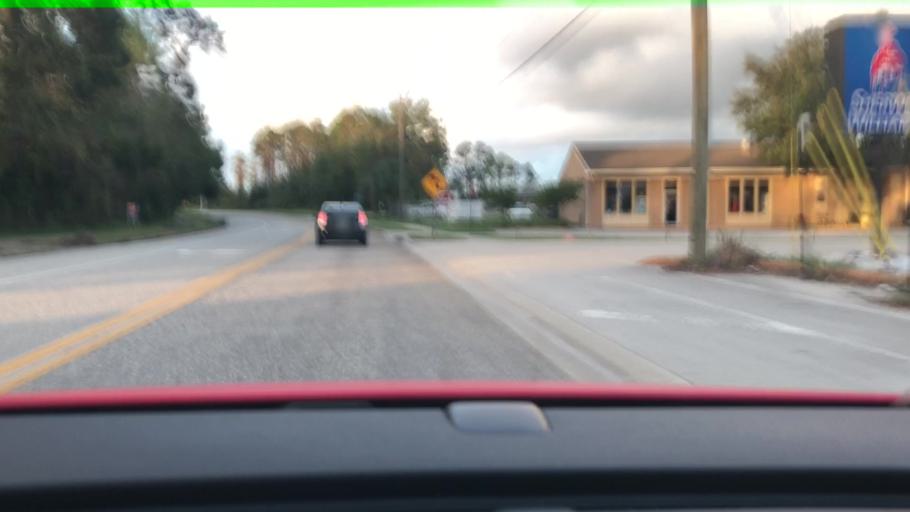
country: US
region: Florida
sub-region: Volusia County
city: South Daytona
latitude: 29.1537
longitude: -81.0215
